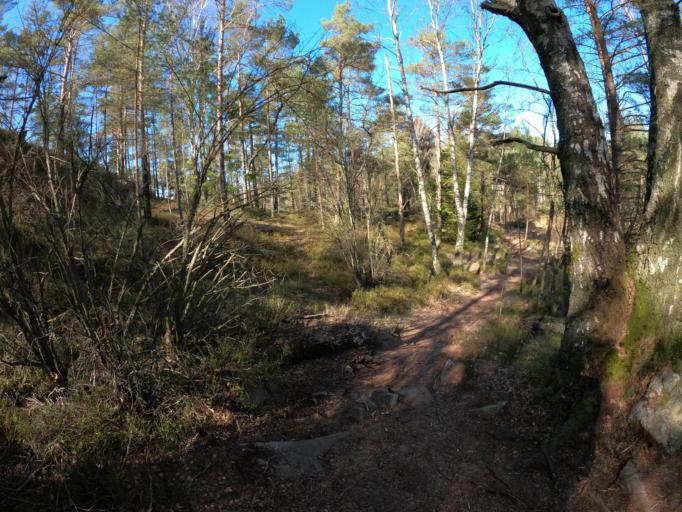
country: SE
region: Vaestra Goetaland
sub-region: Harryda Kommun
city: Molnlycke
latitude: 57.6400
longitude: 12.1145
